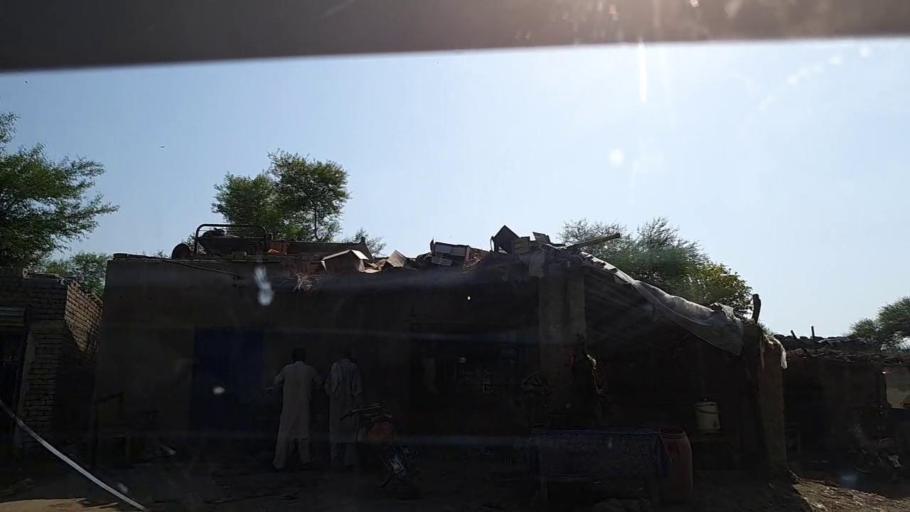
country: PK
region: Sindh
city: Ghauspur
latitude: 28.2014
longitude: 69.0402
